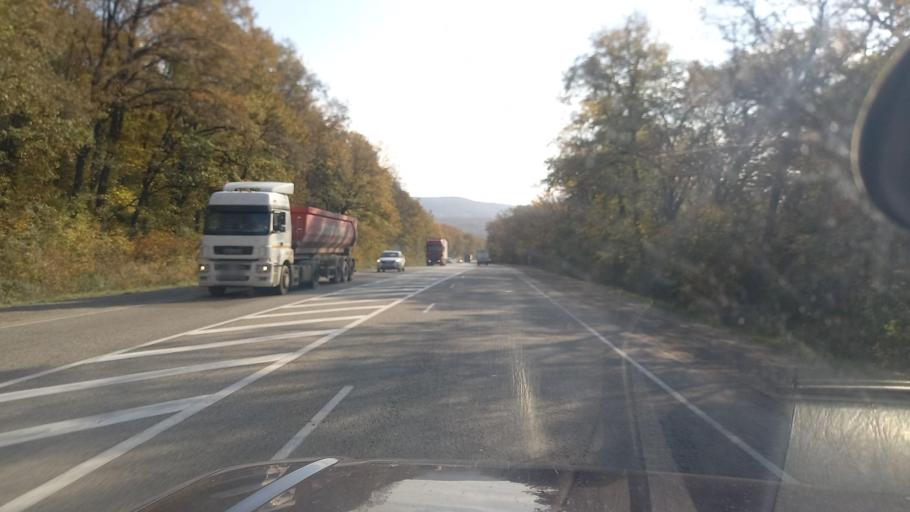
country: RU
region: Krasnodarskiy
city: Verkhnebakanskiy
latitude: 44.8433
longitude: 37.6977
